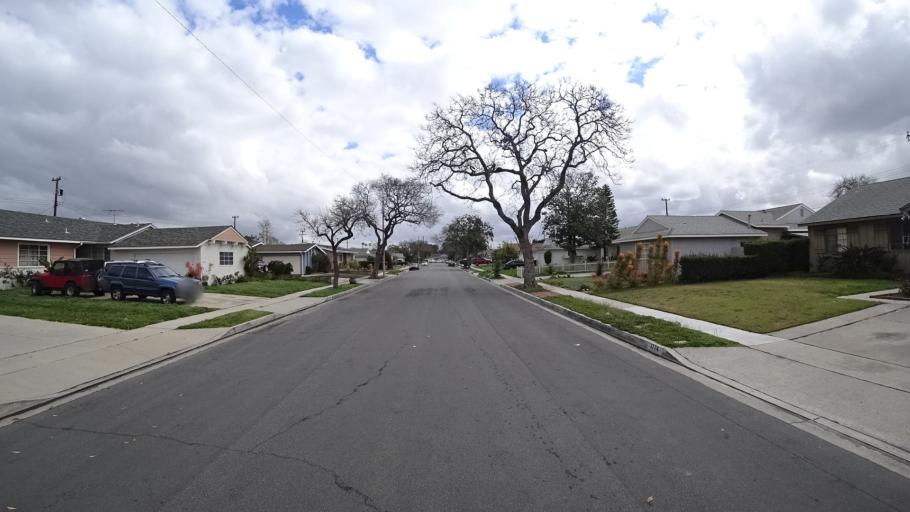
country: US
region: California
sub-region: Orange County
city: Anaheim
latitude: 33.8223
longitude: -117.9450
